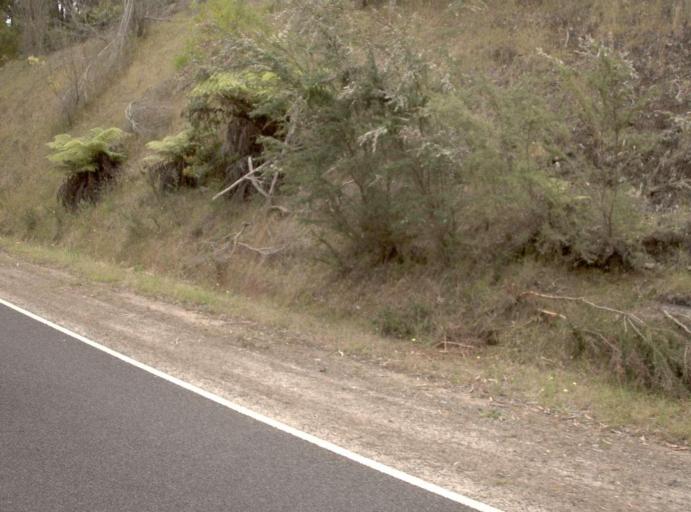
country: AU
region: Victoria
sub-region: Latrobe
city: Traralgon
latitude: -38.4129
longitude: 146.8173
